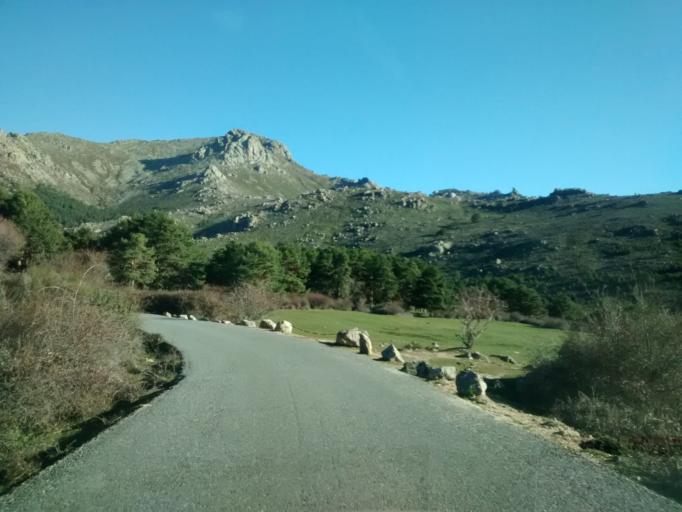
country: ES
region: Madrid
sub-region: Provincia de Madrid
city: Navacerrada
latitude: 40.7467
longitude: -3.9956
